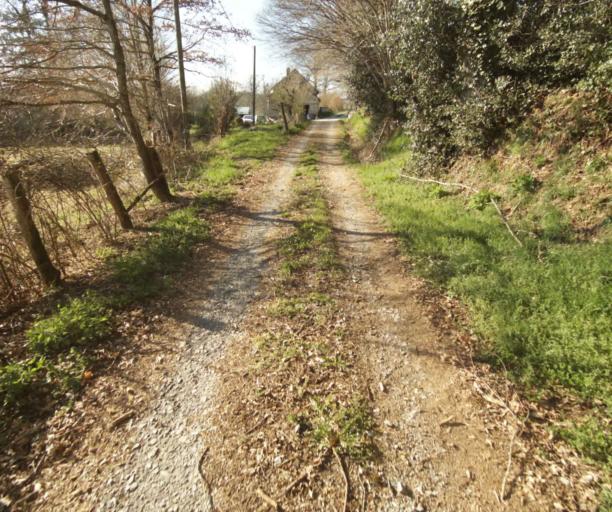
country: FR
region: Limousin
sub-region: Departement de la Correze
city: Chamboulive
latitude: 45.4971
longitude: 1.7249
